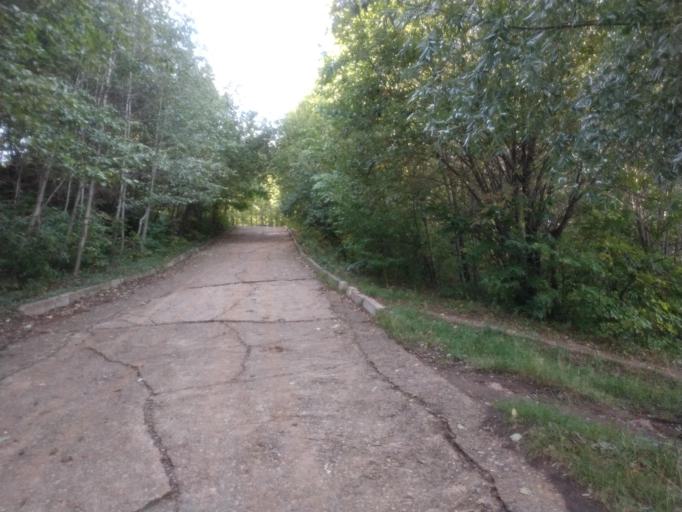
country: RU
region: Chuvashia
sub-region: Cheboksarskiy Rayon
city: Cheboksary
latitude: 56.1546
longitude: 47.1657
